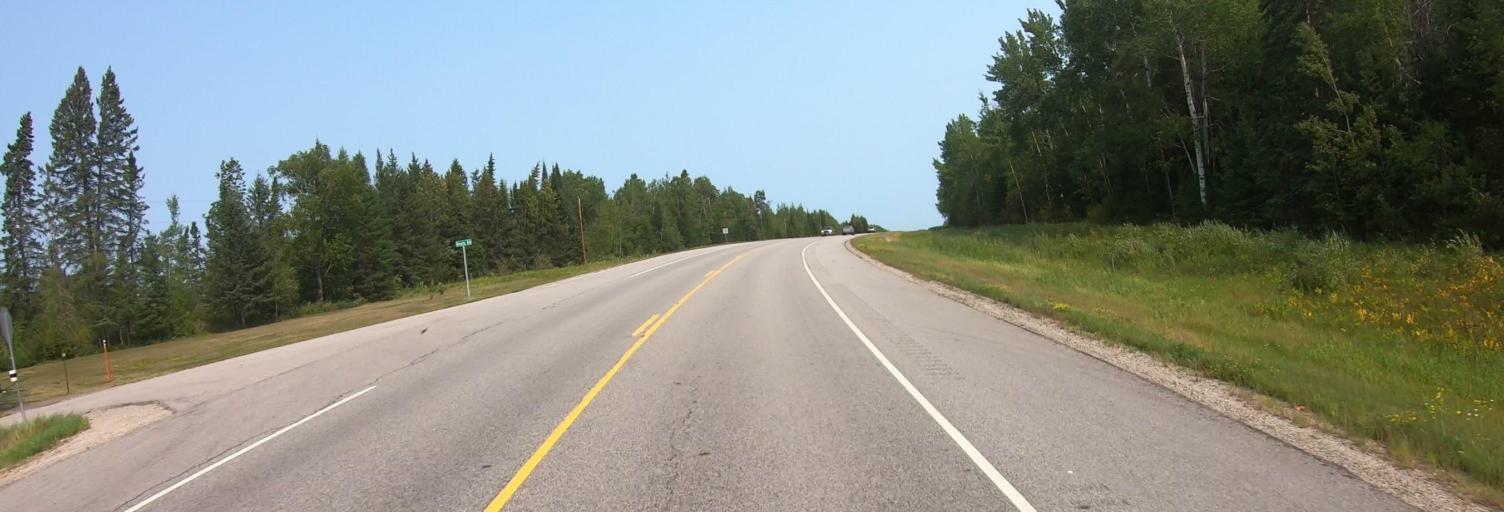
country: CA
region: Ontario
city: Fort Frances
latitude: 48.2974
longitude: -92.9707
